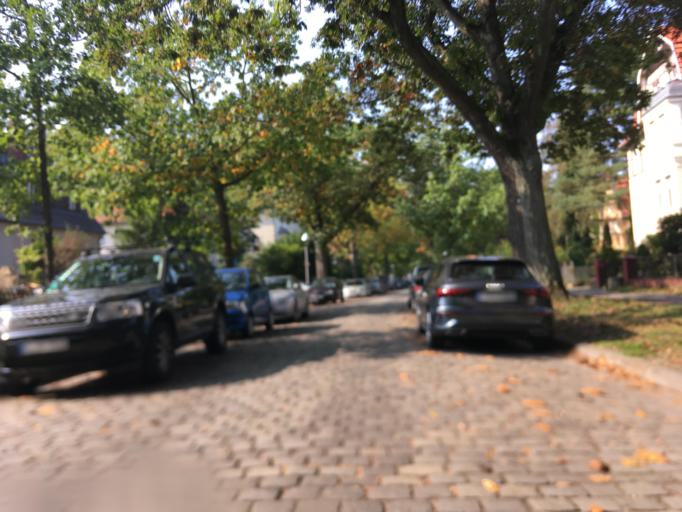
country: DE
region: Berlin
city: Zehlendorf Bezirk
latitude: 52.4370
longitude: 13.2366
